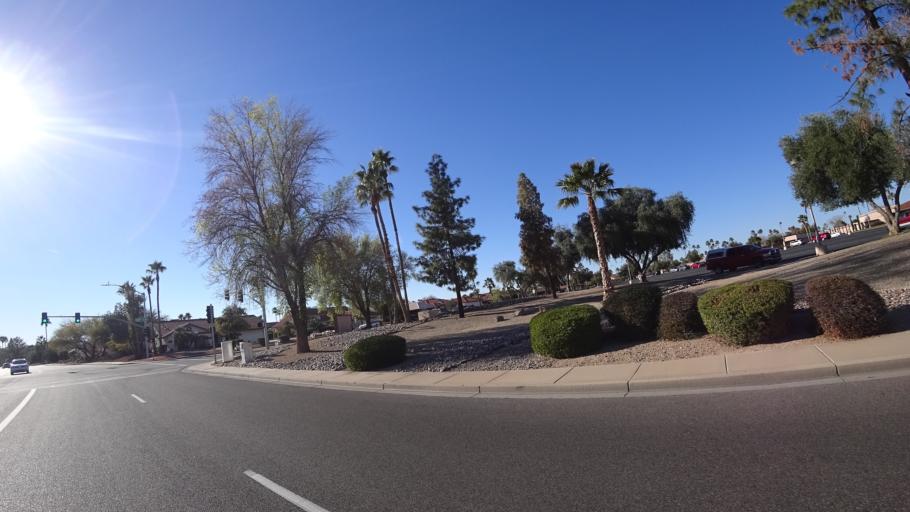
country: US
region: Arizona
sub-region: Maricopa County
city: Sun City West
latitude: 33.6716
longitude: -112.3519
